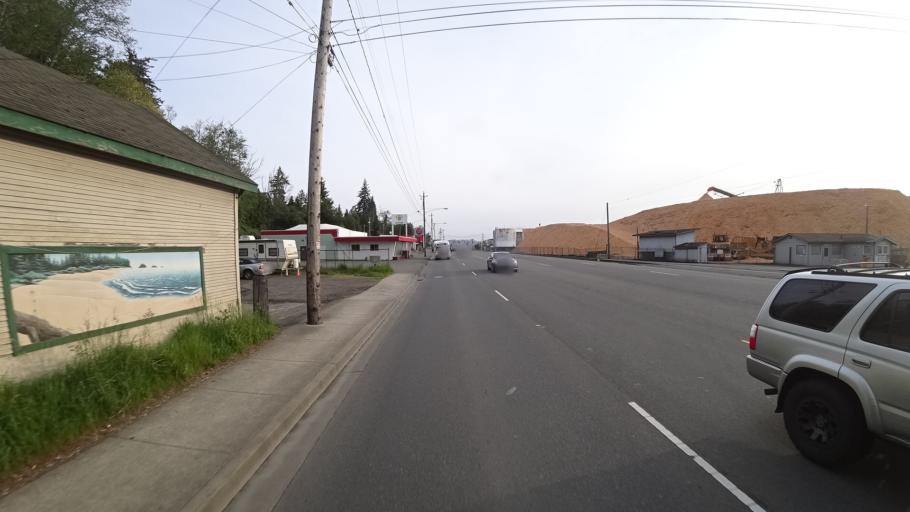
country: US
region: Oregon
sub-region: Coos County
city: North Bend
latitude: 43.3890
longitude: -124.2206
